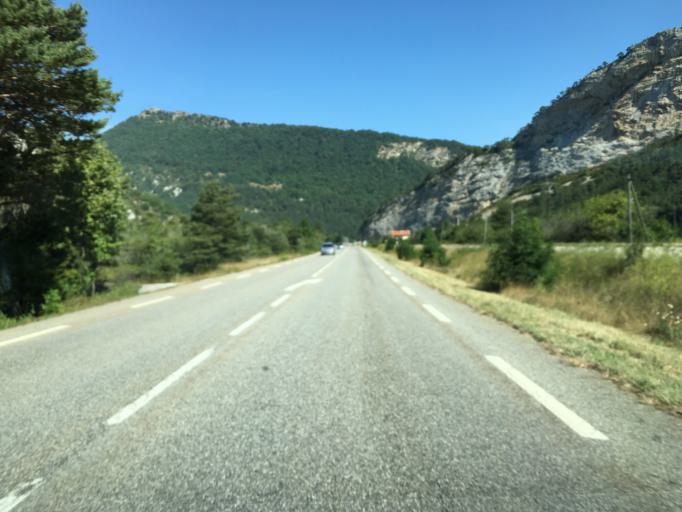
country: FR
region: Provence-Alpes-Cote d'Azur
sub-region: Departement des Hautes-Alpes
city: Veynes
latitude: 44.6330
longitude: 5.6962
